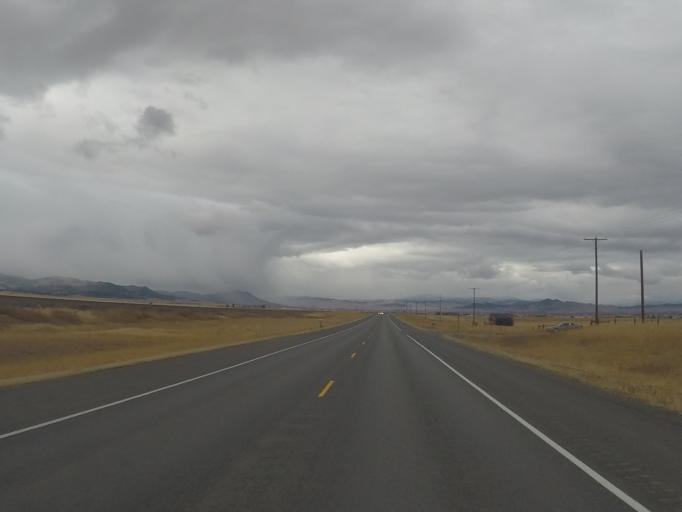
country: US
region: Montana
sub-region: Lewis and Clark County
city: East Helena
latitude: 46.5841
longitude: -111.8592
